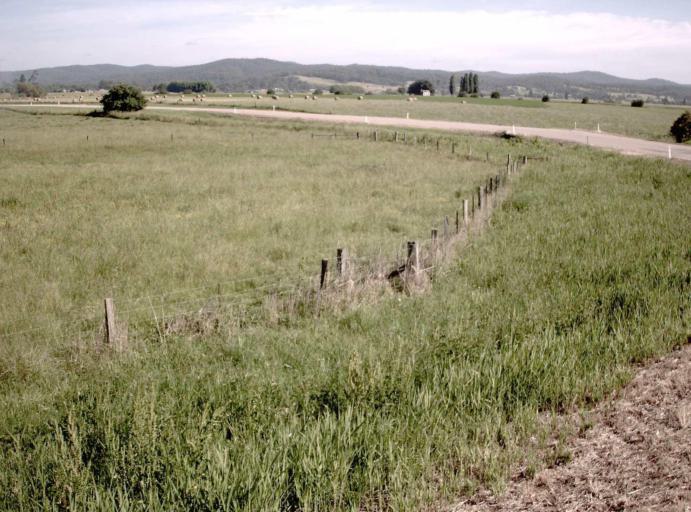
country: AU
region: Victoria
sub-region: East Gippsland
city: Lakes Entrance
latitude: -37.7409
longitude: 147.8182
